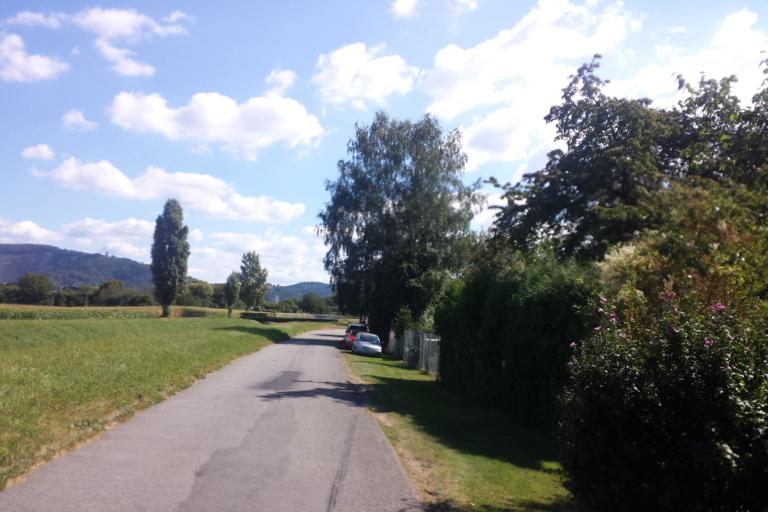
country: DE
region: Baden-Wuerttemberg
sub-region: Karlsruhe Region
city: Weinheim
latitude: 49.5638
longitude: 8.6460
